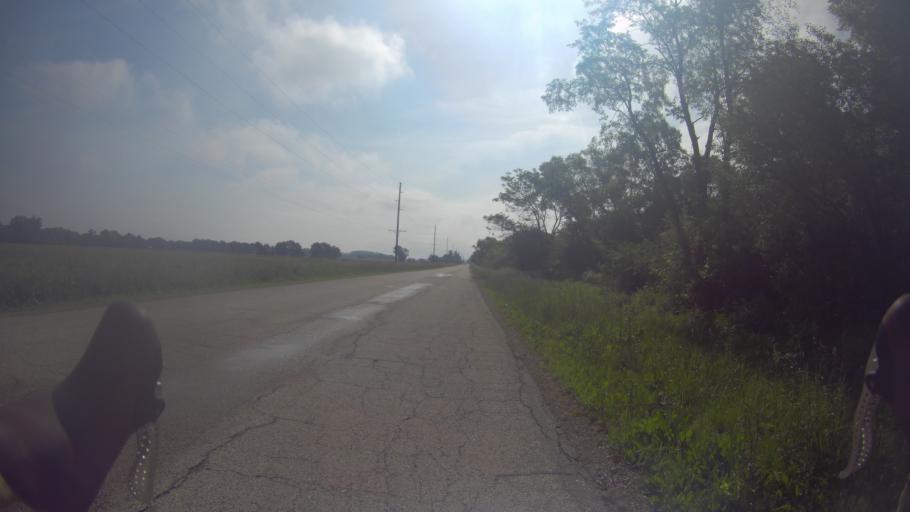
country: US
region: Wisconsin
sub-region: Dane County
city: McFarland
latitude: 42.9913
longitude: -89.2215
